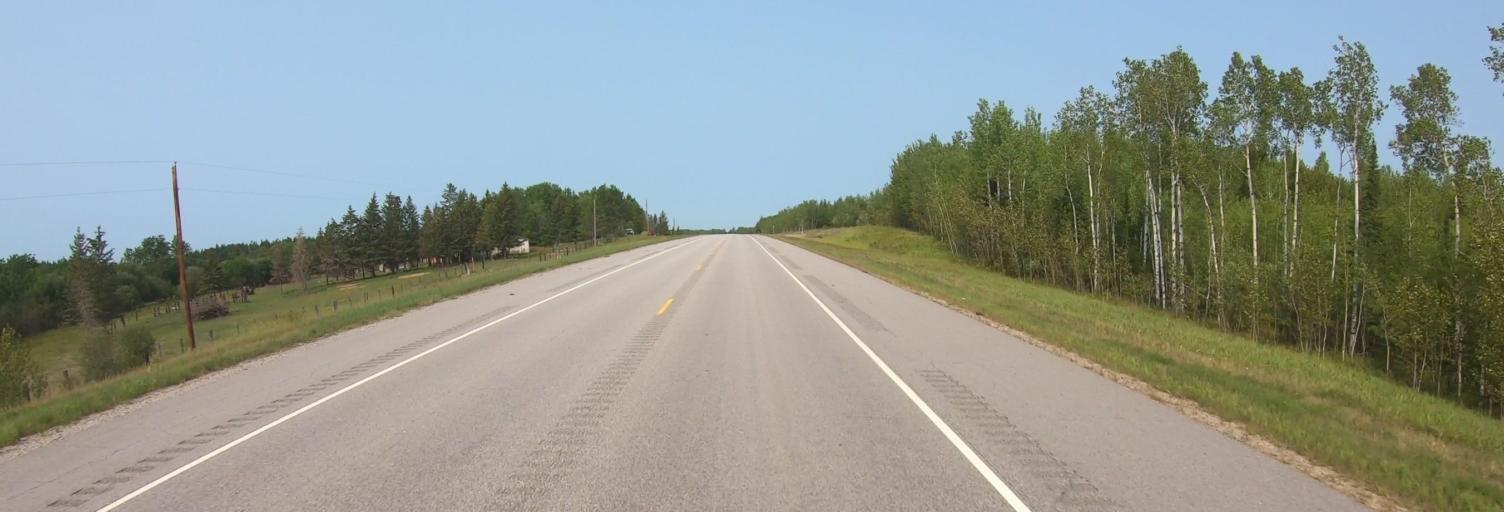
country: CA
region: Ontario
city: Fort Frances
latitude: 48.4164
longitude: -93.2125
